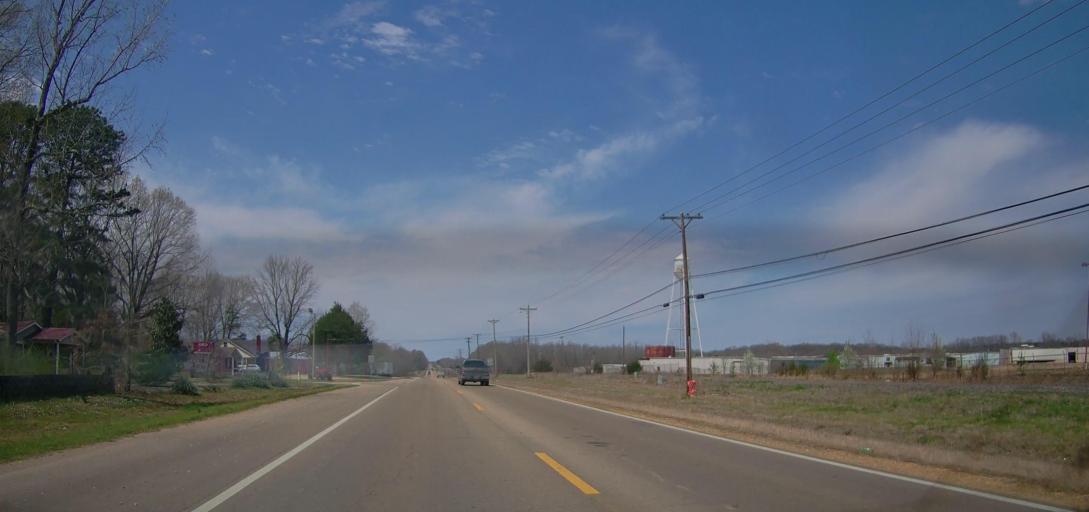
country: US
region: Mississippi
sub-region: Union County
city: New Albany
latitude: 34.5153
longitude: -89.0445
